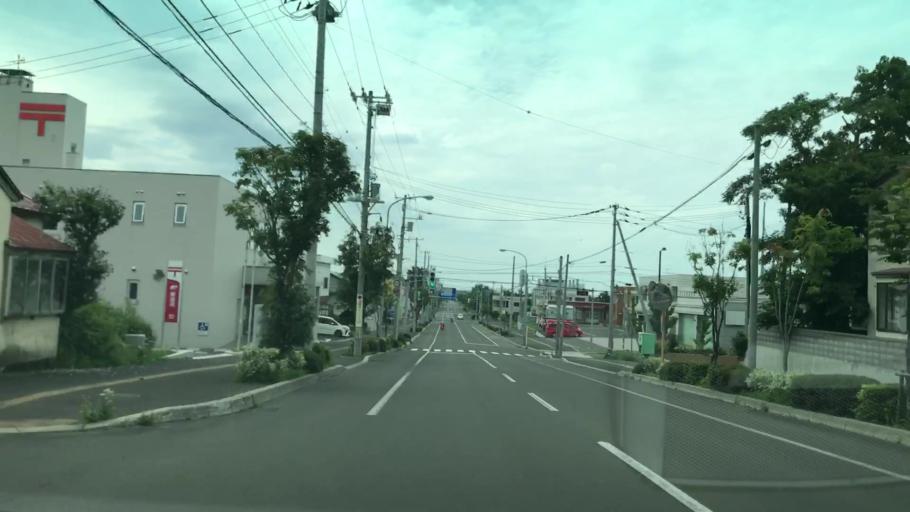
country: JP
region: Hokkaido
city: Iwanai
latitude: 42.9792
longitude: 140.5129
